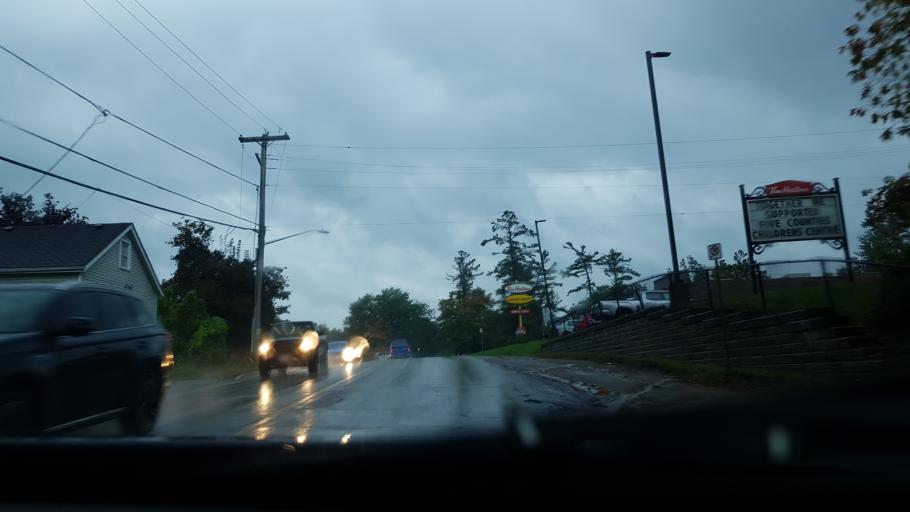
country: CA
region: Ontario
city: Peterborough
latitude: 44.3762
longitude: -78.3862
